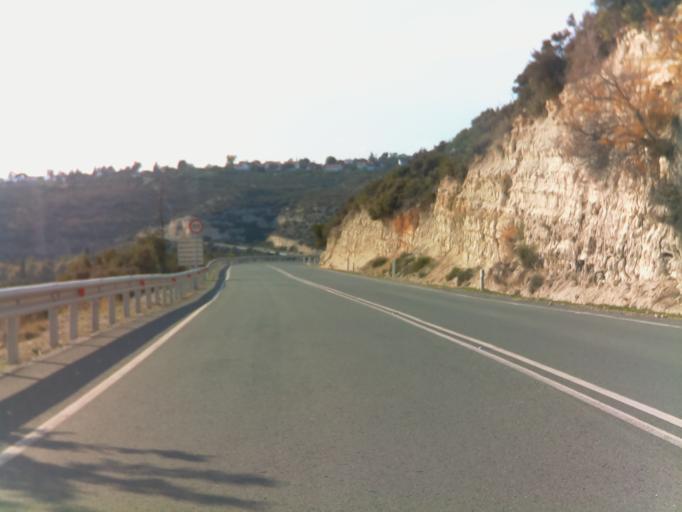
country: CY
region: Limassol
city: Sotira
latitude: 34.6724
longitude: 32.8255
